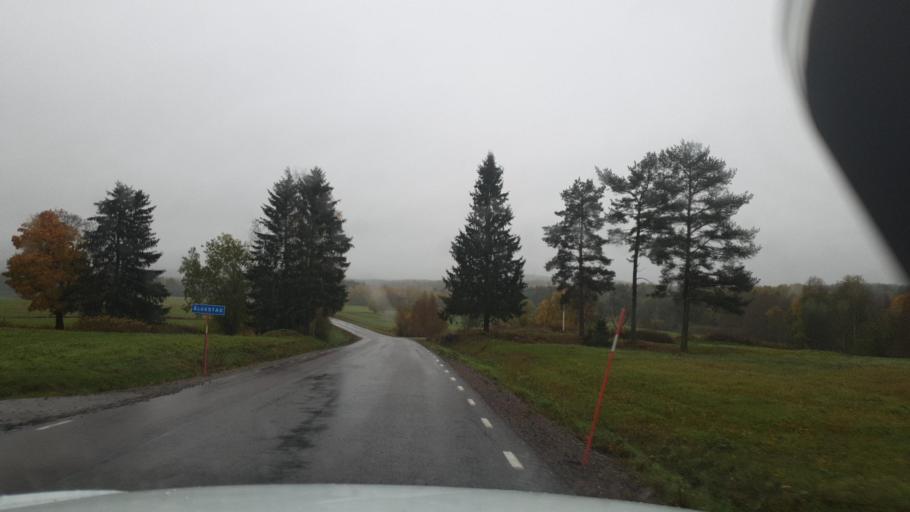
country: SE
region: Vaermland
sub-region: Eda Kommun
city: Charlottenberg
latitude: 59.7851
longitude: 12.1594
